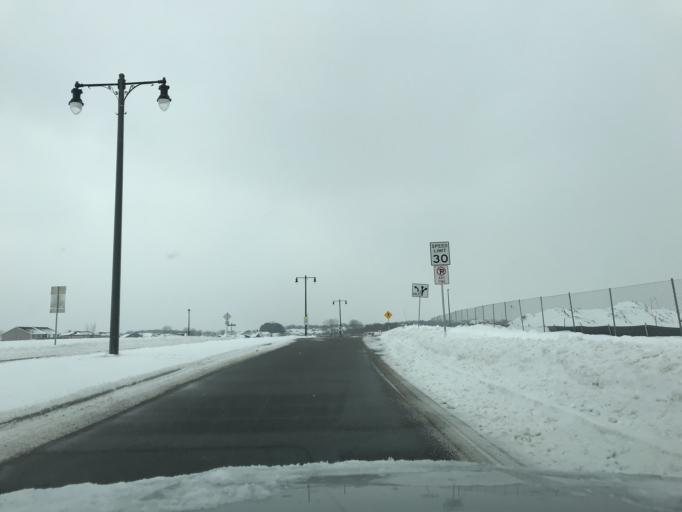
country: US
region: Wisconsin
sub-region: Dane County
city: Sun Prairie
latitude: 43.1763
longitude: -89.2665
